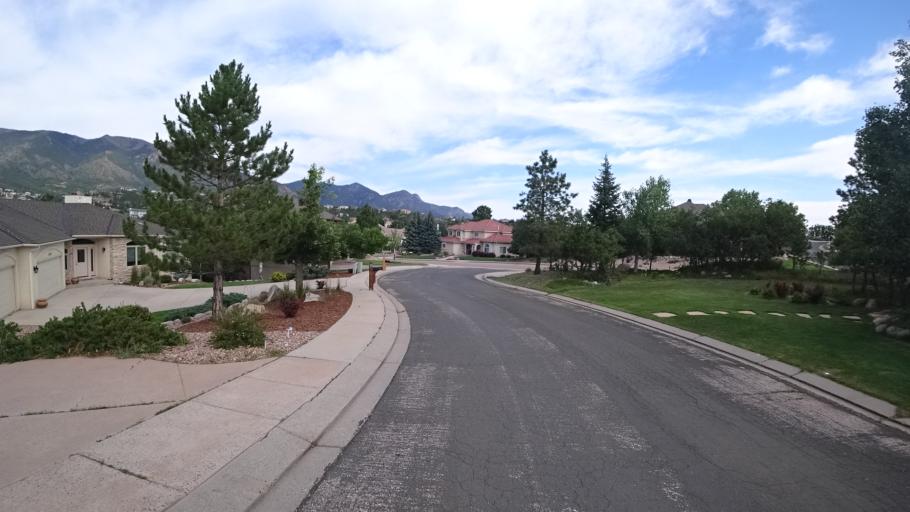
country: US
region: Colorado
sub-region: El Paso County
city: Air Force Academy
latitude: 38.9470
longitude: -104.8629
